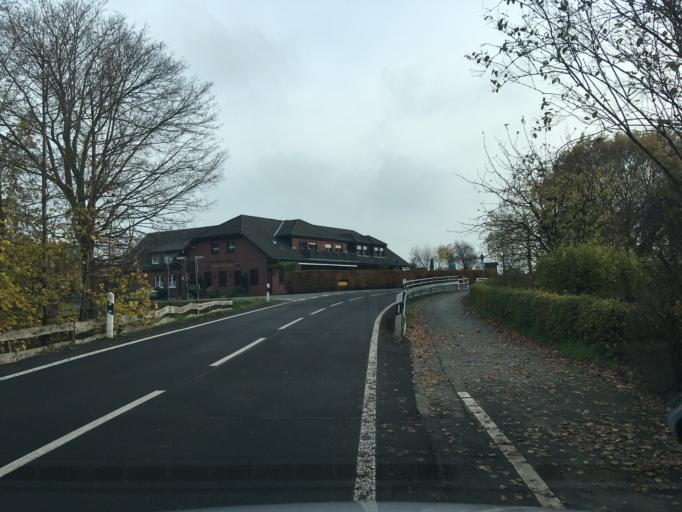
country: DE
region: North Rhine-Westphalia
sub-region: Regierungsbezirk Munster
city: Velen
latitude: 51.9173
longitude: 6.9624
